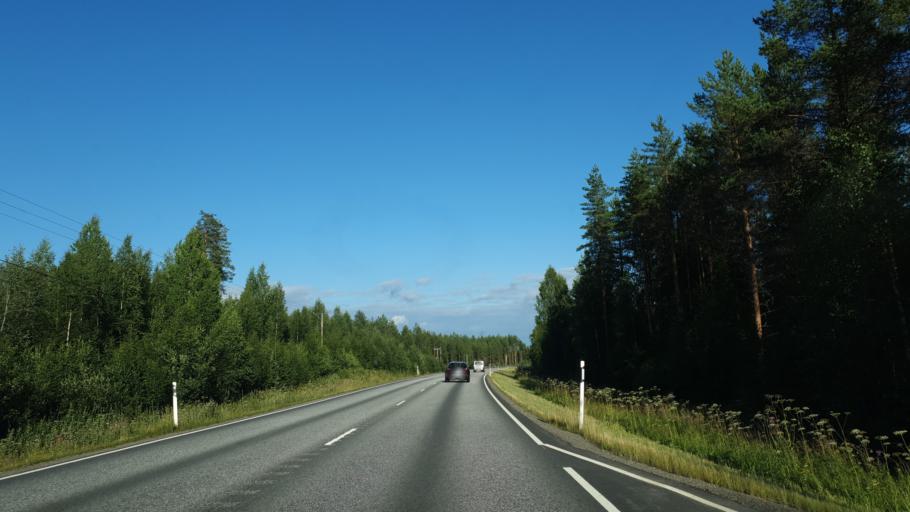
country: FI
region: North Karelia
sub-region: Joensuu
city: Outokumpu
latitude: 62.5322
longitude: 28.9713
